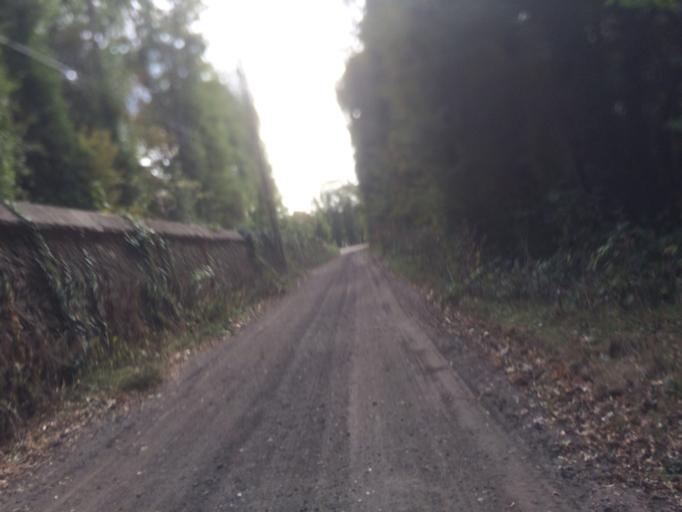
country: FR
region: Ile-de-France
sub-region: Departement des Yvelines
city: Bonnelles
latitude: 48.6120
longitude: 2.0191
